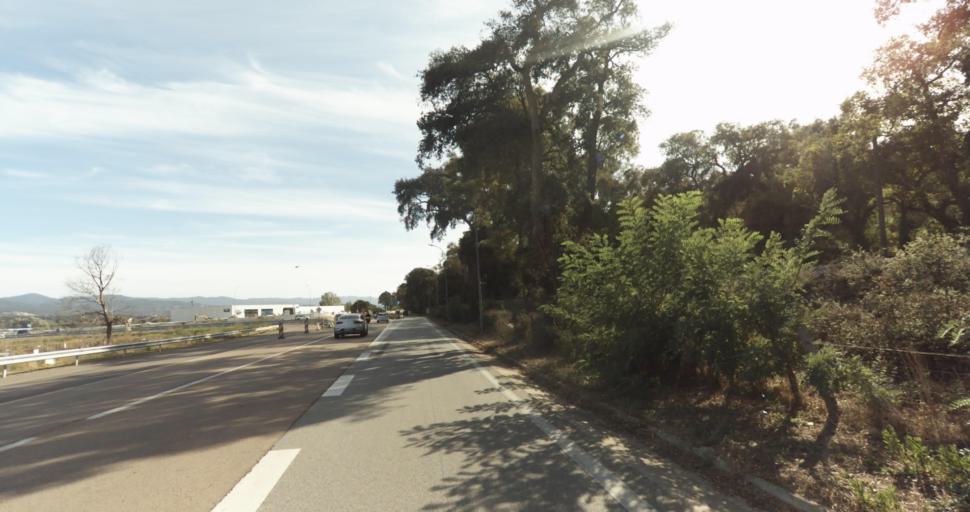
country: FR
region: Corsica
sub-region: Departement de la Corse-du-Sud
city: Afa
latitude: 41.9329
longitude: 8.8022
